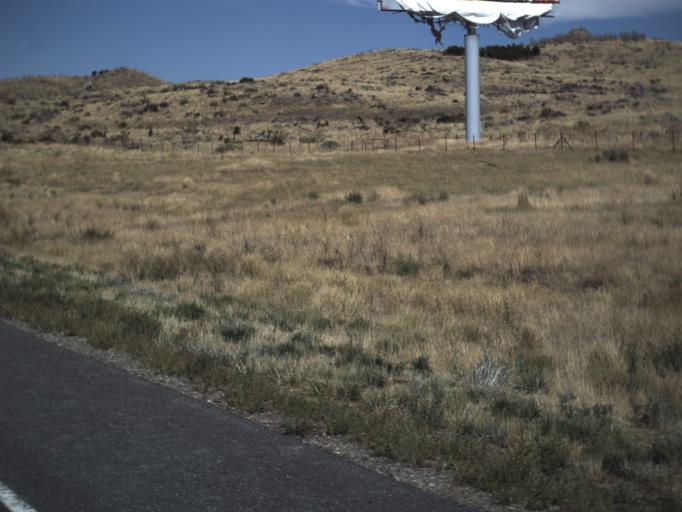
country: US
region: Utah
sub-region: Beaver County
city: Beaver
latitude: 38.6204
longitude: -112.6093
